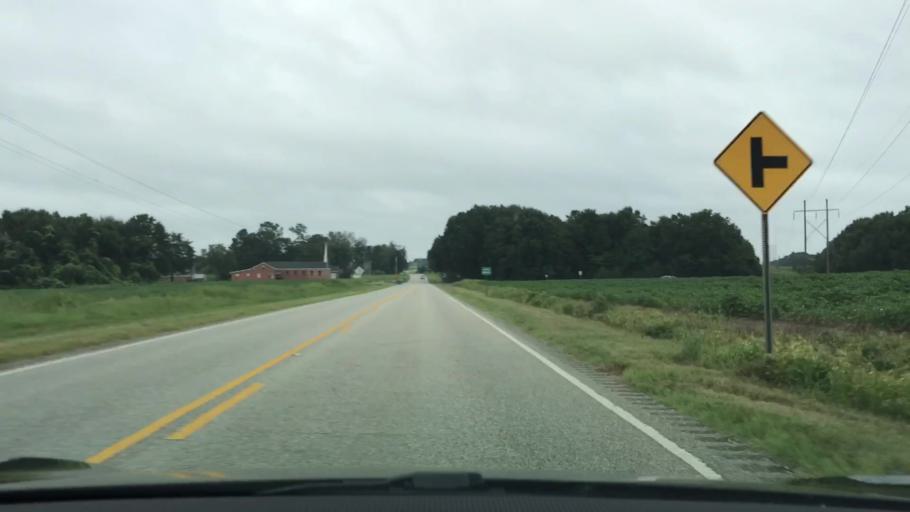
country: US
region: Alabama
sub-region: Coffee County
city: Elba
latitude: 31.3399
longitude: -86.1311
